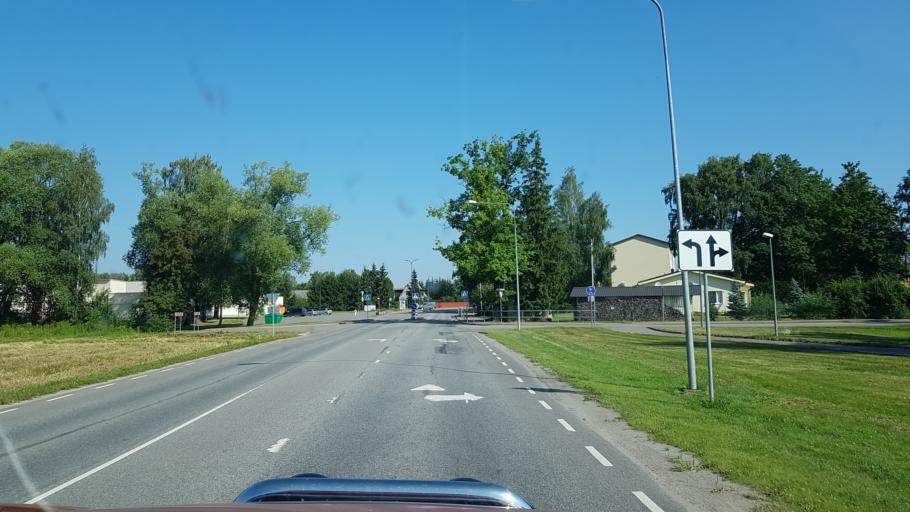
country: EE
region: Tartu
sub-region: Tartu linn
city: Tartu
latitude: 58.4184
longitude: 26.7632
